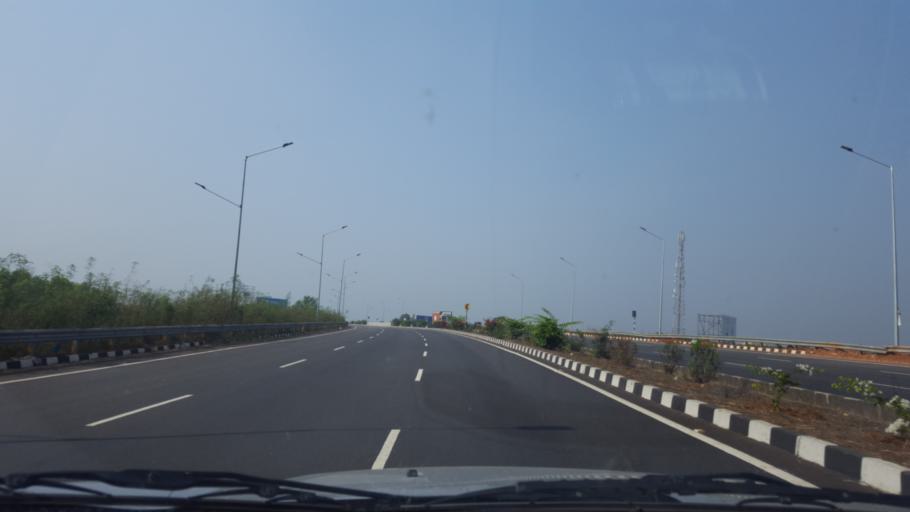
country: IN
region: Andhra Pradesh
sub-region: Vishakhapatnam
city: Bhimunipatnam
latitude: 17.9630
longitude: 83.4215
